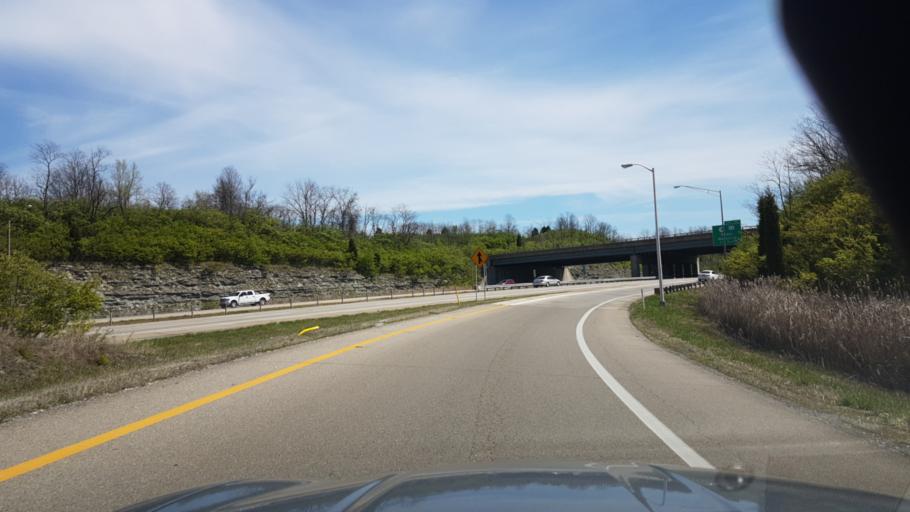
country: US
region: Kentucky
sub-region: Kenton County
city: Taylor Mill
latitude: 39.0217
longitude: -84.5140
